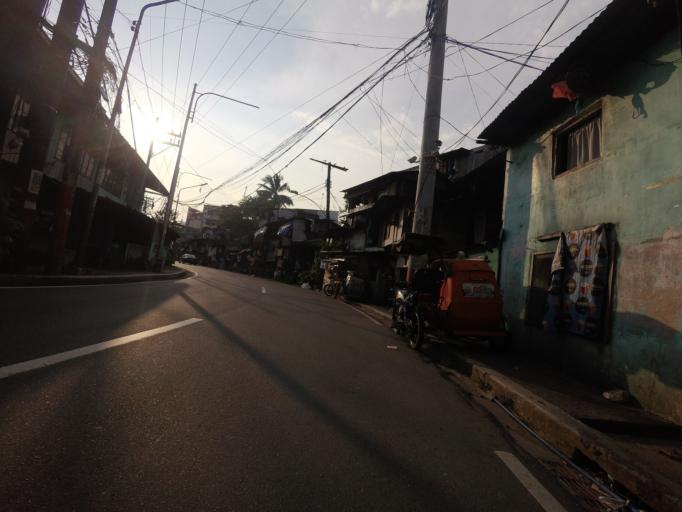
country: PH
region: Metro Manila
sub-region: San Juan
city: San Juan
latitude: 14.6022
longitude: 121.0219
